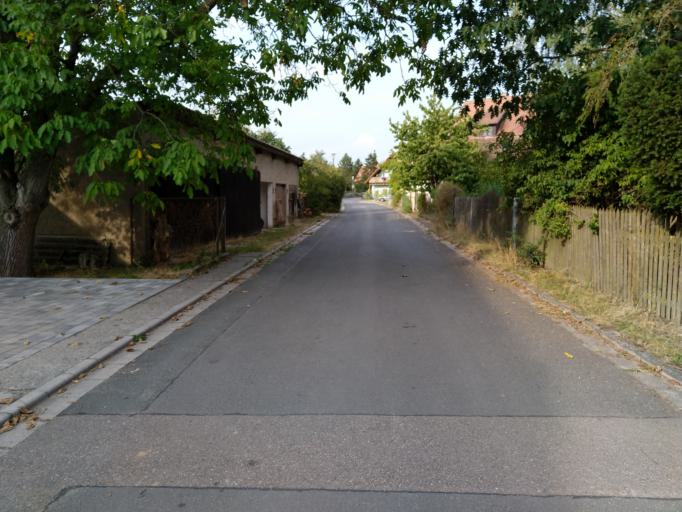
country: DE
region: Bavaria
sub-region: Regierungsbezirk Mittelfranken
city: Hagenbuchach
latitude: 49.5344
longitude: 10.7910
